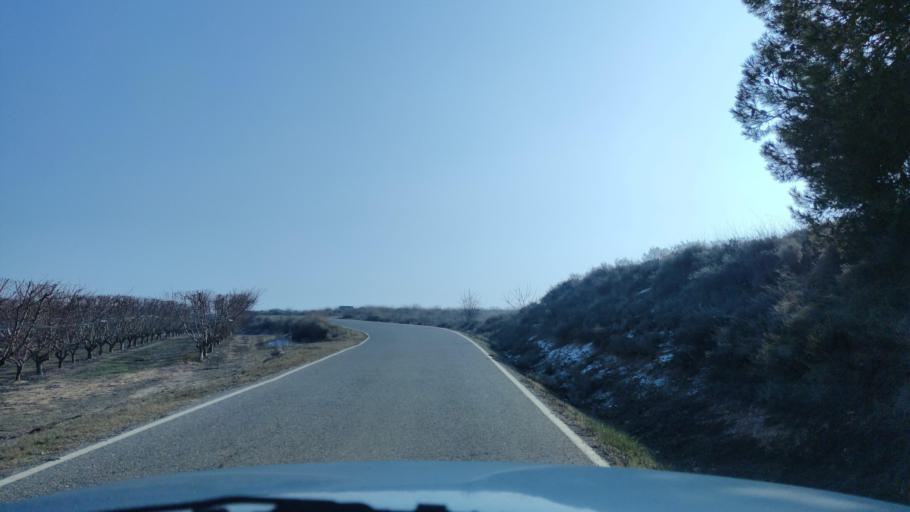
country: ES
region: Catalonia
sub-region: Provincia de Lleida
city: Sunyer
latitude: 41.5303
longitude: 0.5779
